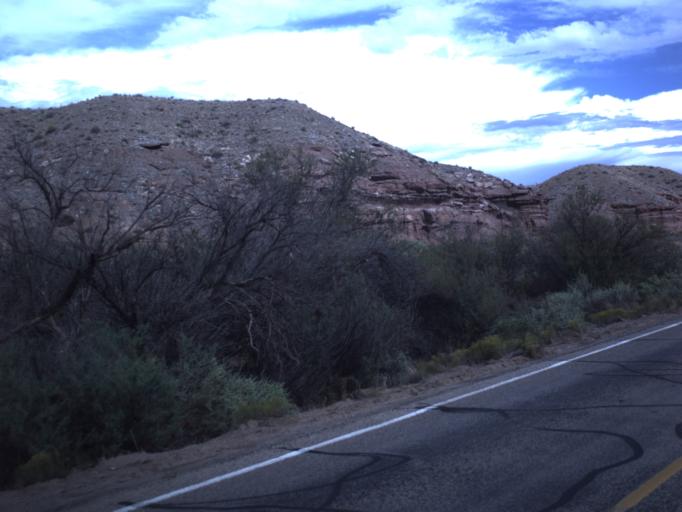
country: US
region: Colorado
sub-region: Montezuma County
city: Towaoc
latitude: 37.2225
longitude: -109.2024
